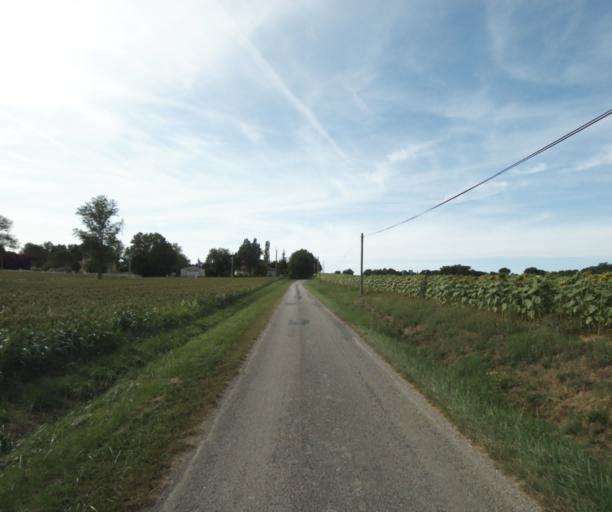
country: FR
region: Midi-Pyrenees
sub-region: Departement du Tarn
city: Puylaurens
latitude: 43.5369
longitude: 2.0525
